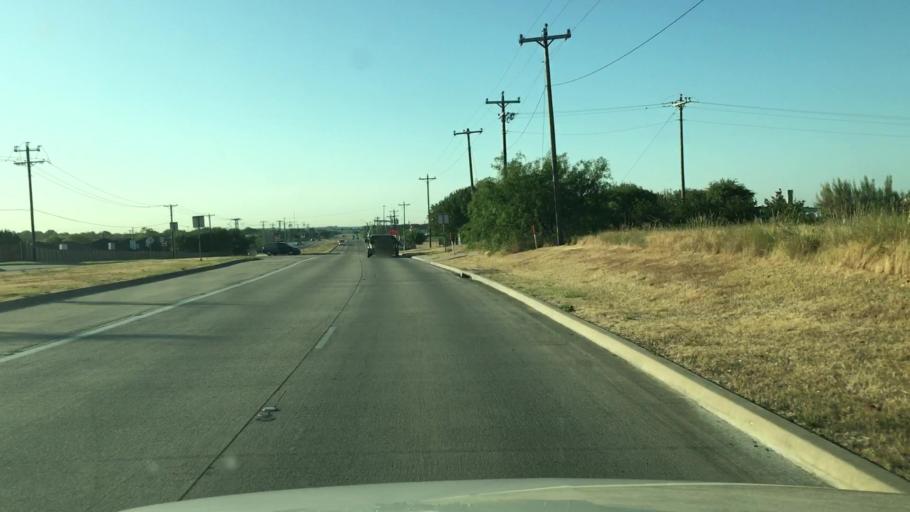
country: US
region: Texas
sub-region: Tarrant County
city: Crowley
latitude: 32.5419
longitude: -97.3643
